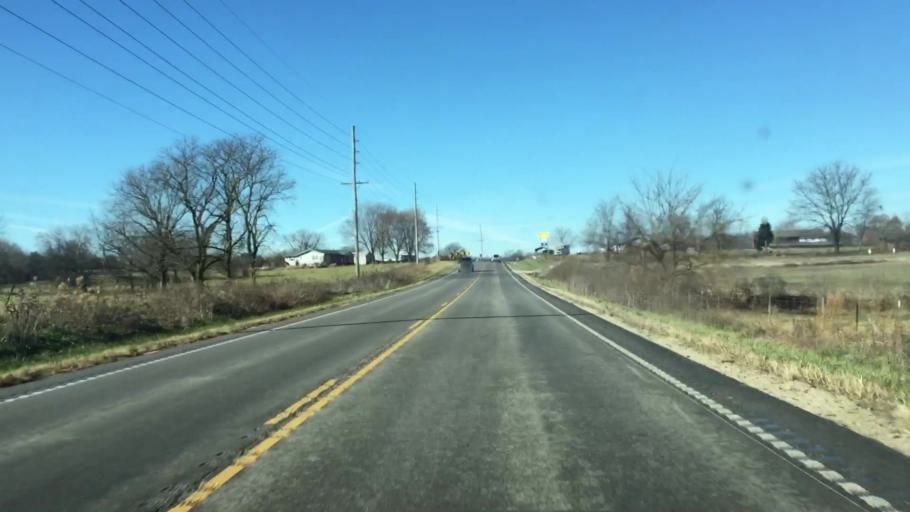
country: US
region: Missouri
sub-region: Miller County
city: Eldon
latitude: 38.3738
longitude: -92.6520
